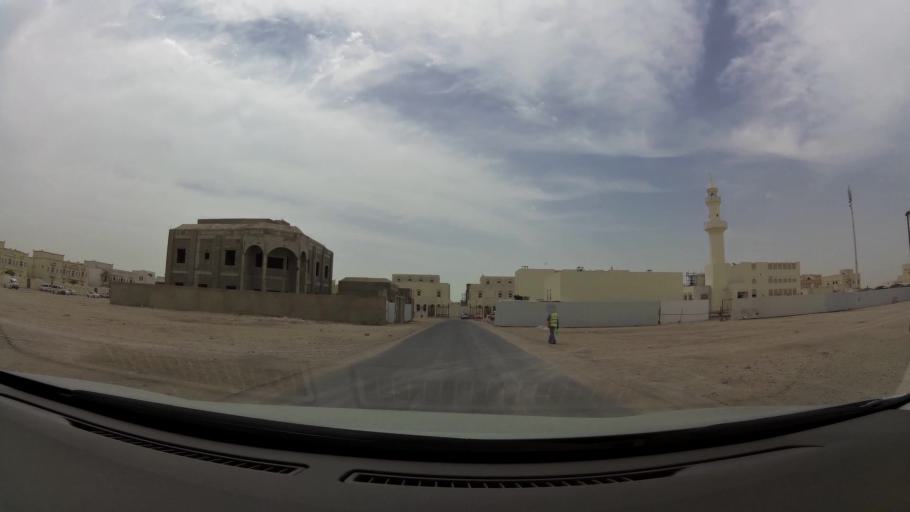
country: QA
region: Baladiyat ad Dawhah
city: Doha
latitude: 25.2081
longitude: 51.4649
